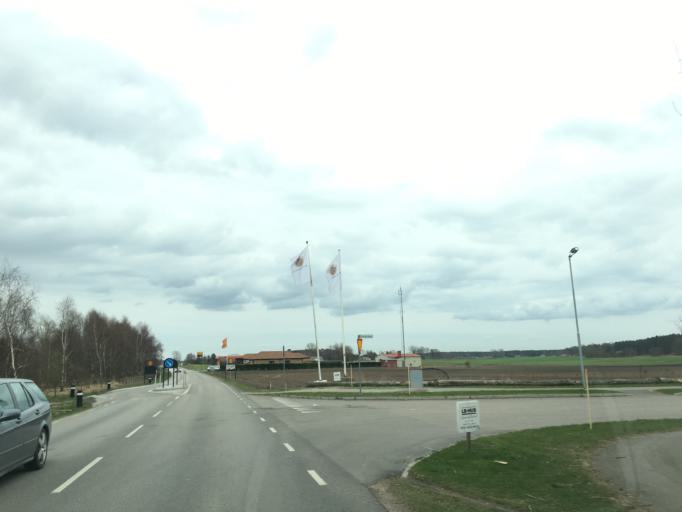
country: SE
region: Skane
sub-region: Landskrona
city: Asmundtorp
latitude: 55.8505
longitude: 12.9321
